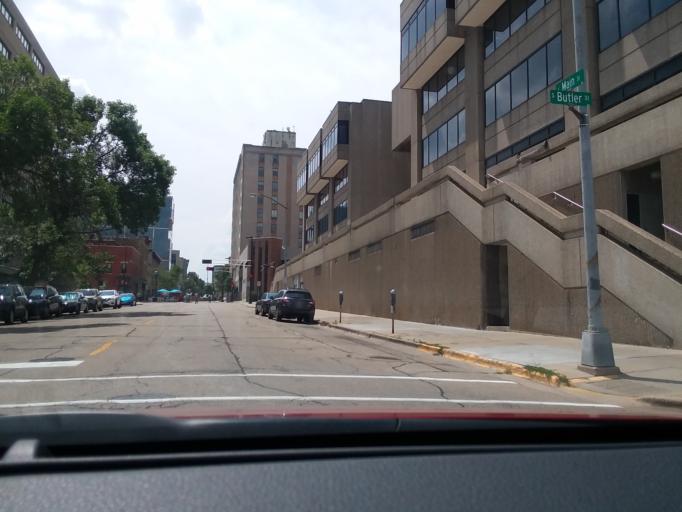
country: US
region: Wisconsin
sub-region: Dane County
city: Madison
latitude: 43.0759
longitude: -89.3802
